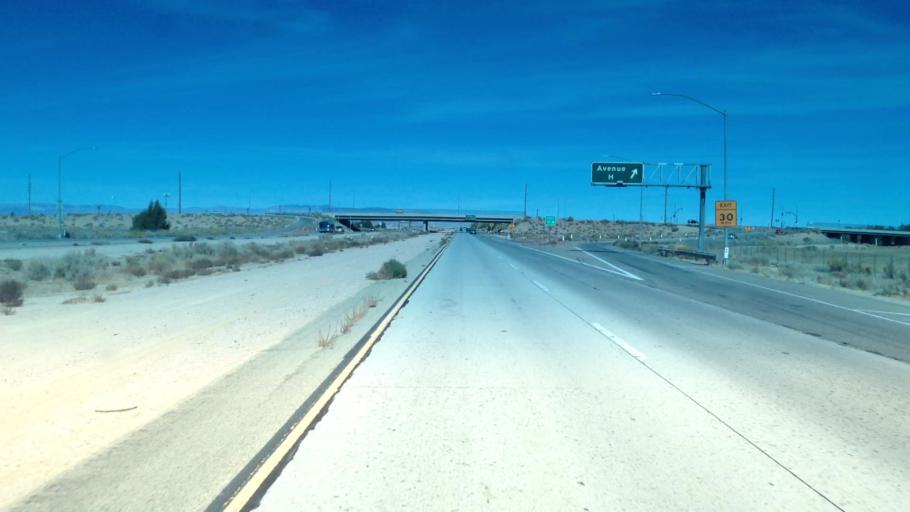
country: US
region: California
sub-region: Los Angeles County
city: Lancaster
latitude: 34.7148
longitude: -118.1700
